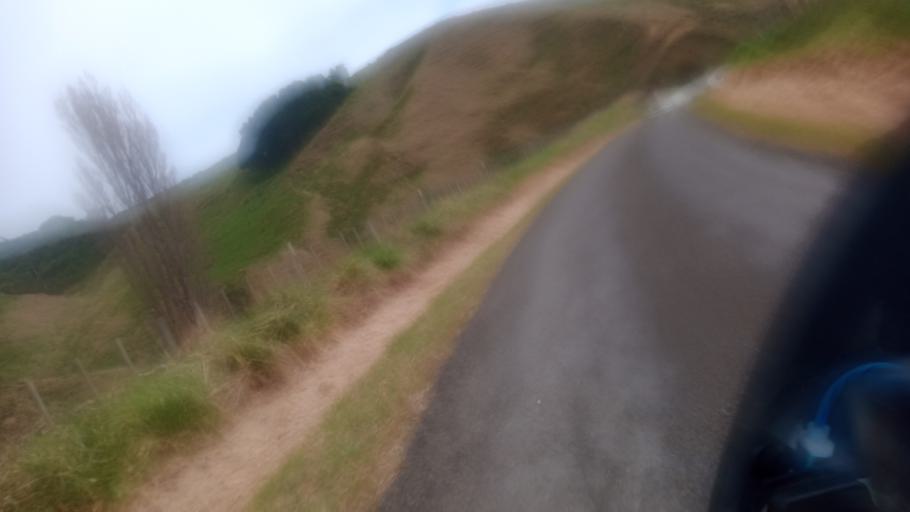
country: NZ
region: Gisborne
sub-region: Gisborne District
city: Gisborne
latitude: -38.5872
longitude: 178.1804
